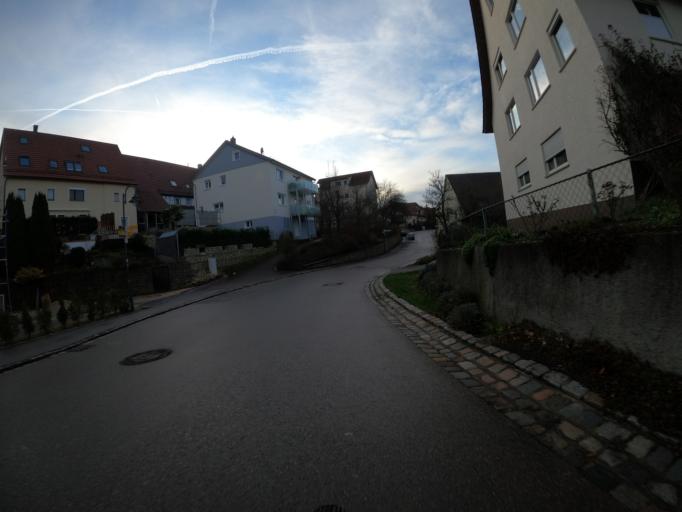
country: DE
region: Baden-Wuerttemberg
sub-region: Regierungsbezirk Stuttgart
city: Zell unter Aichelberg
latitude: 48.6472
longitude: 9.5738
